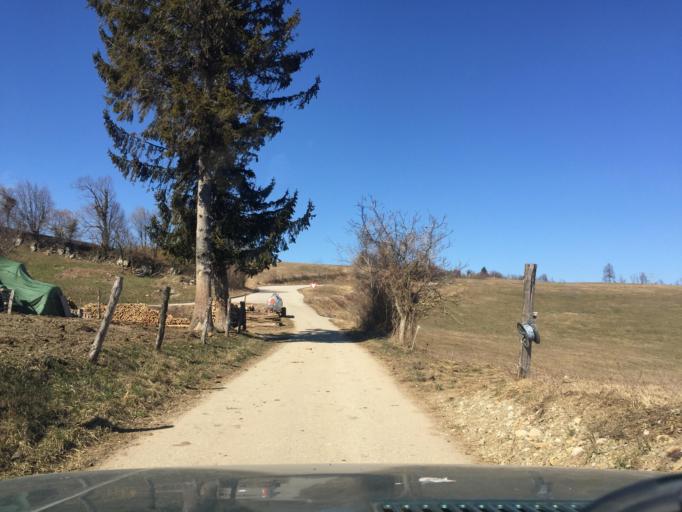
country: SI
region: Kanal
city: Kanal
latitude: 46.0794
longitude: 13.6620
